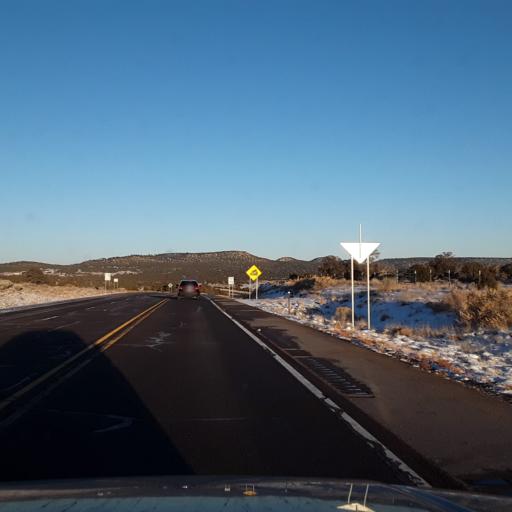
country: US
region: New Mexico
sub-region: Lincoln County
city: Carrizozo
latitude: 34.2372
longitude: -105.6100
